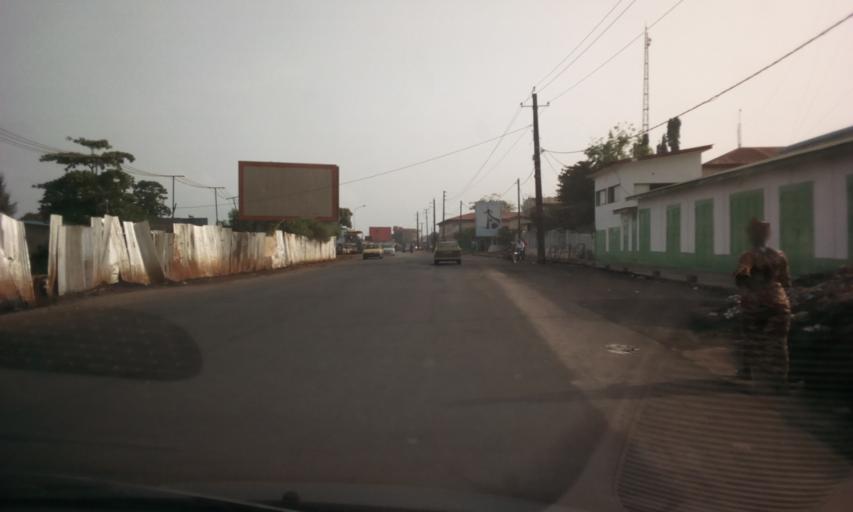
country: GN
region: Conakry
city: Conakry
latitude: 9.6073
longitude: -13.6486
